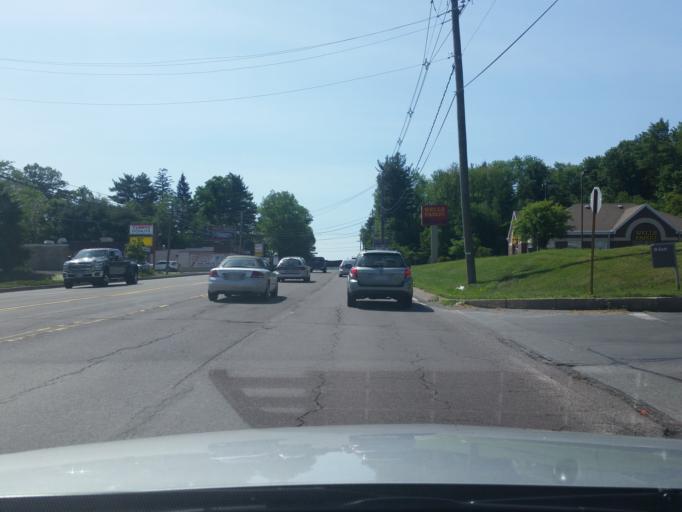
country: US
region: Pennsylvania
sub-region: Luzerne County
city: Shavertown
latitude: 41.3279
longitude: -75.9472
